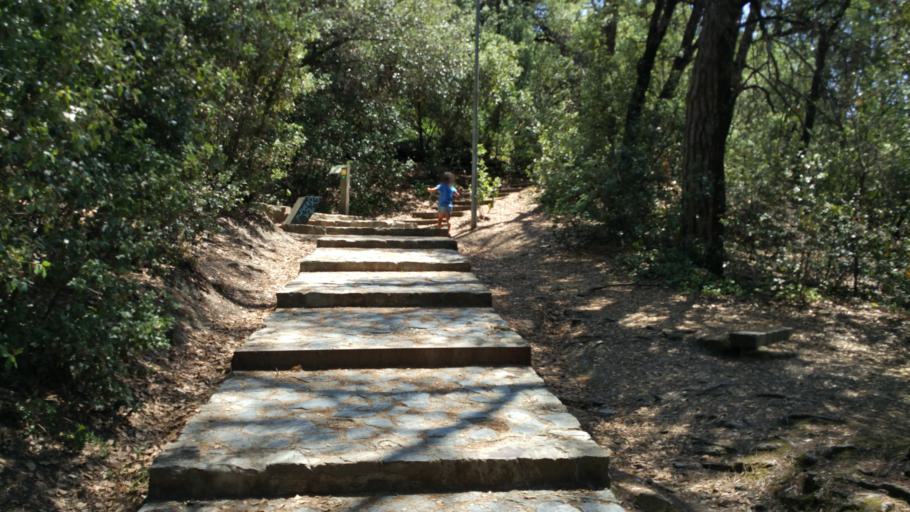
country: ES
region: Catalonia
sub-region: Provincia de Barcelona
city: Sant Just Desvern
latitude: 41.4197
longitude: 2.0983
